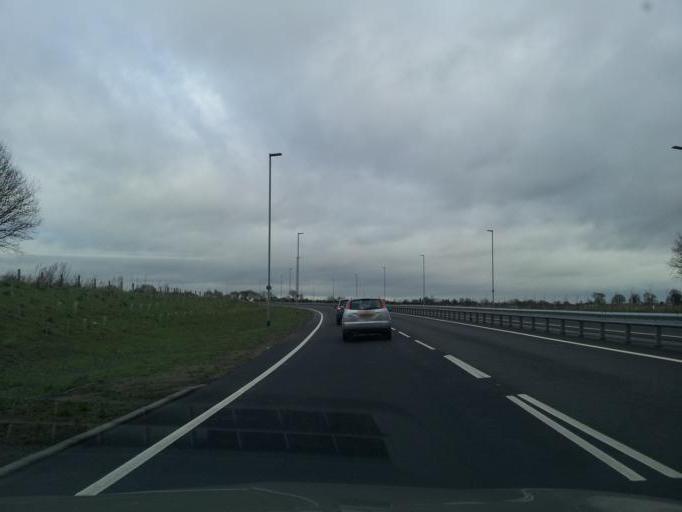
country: GB
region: England
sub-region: Norfolk
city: Surlingham
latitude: 52.6284
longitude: 1.3855
